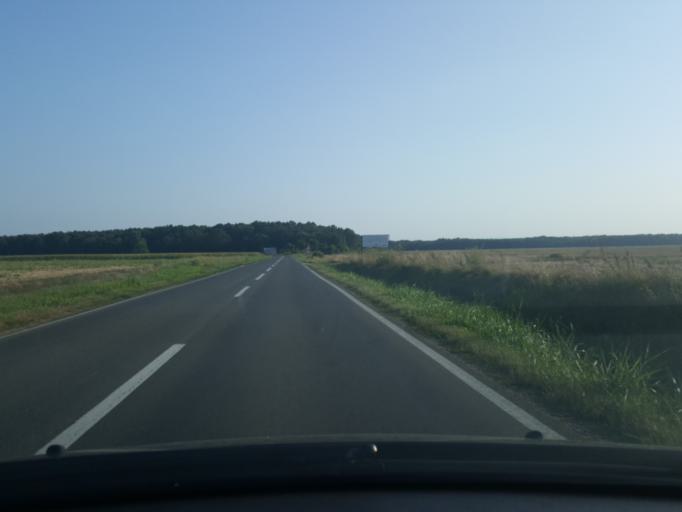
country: RS
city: Hrtkovci
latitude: 44.8470
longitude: 19.7684
